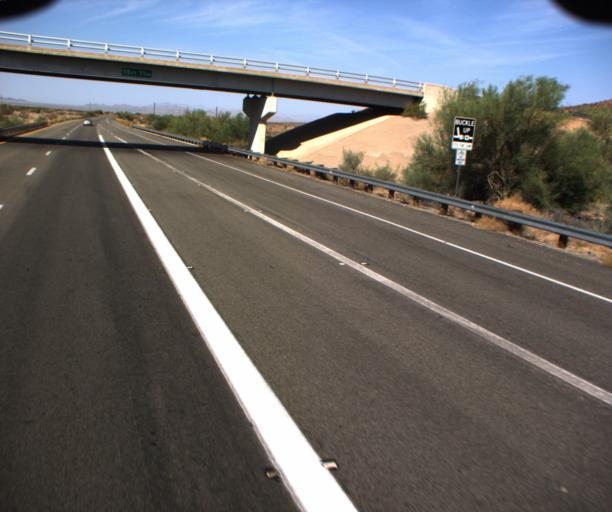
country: US
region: Arizona
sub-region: Mohave County
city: Desert Hills
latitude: 34.7955
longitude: -114.1606
